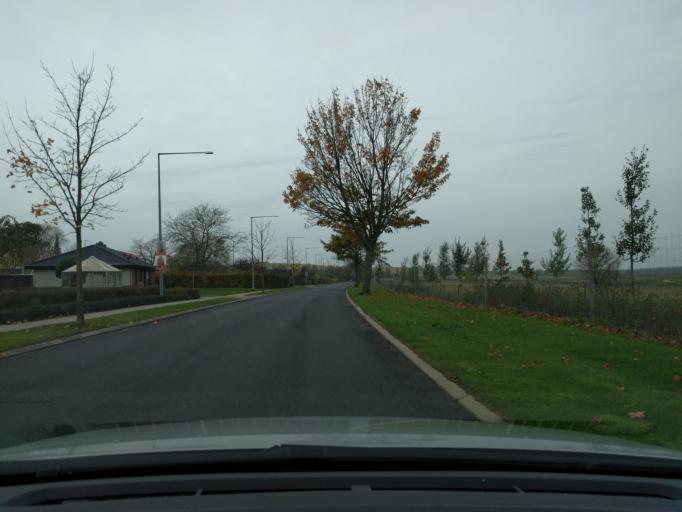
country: DK
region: South Denmark
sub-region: Kerteminde Kommune
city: Kerteminde
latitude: 55.4582
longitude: 10.6414
